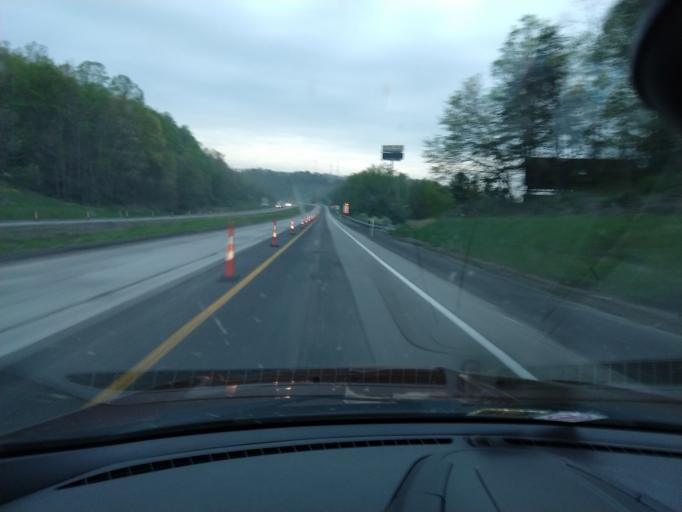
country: US
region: West Virginia
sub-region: Braxton County
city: Sutton
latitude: 38.7133
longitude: -80.6589
